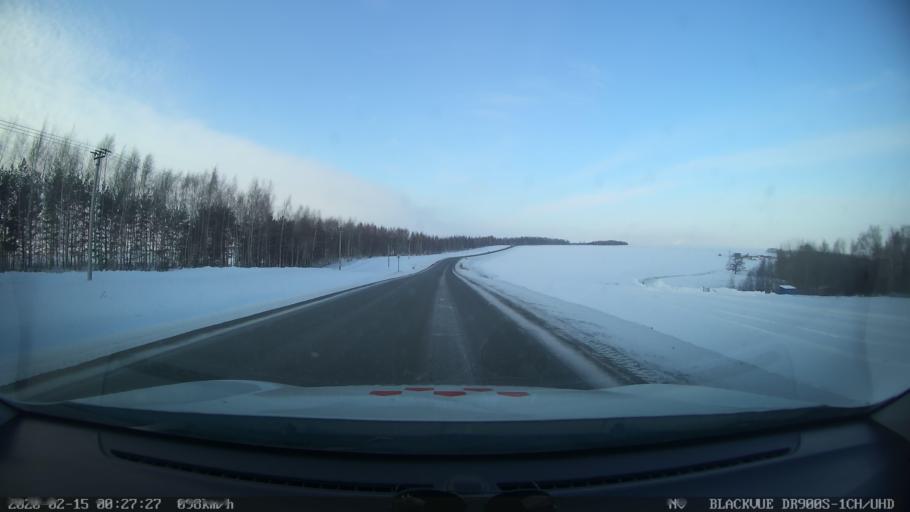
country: RU
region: Tatarstan
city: Verkhniy Uslon
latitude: 55.6283
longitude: 48.8742
